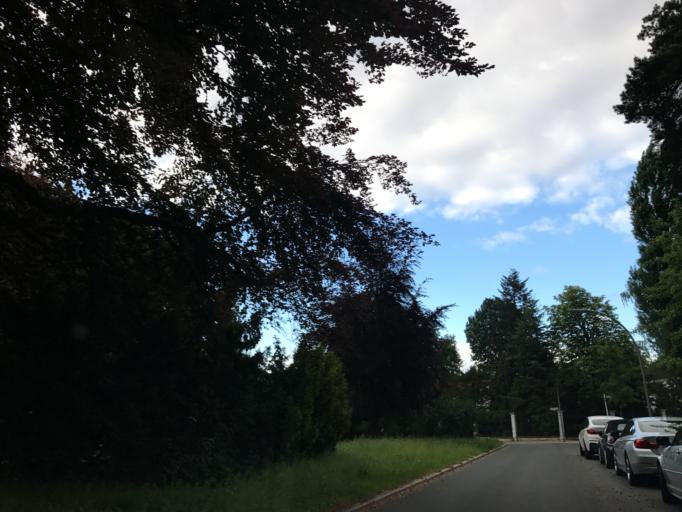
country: DE
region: Berlin
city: Halensee
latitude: 52.4895
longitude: 13.2820
